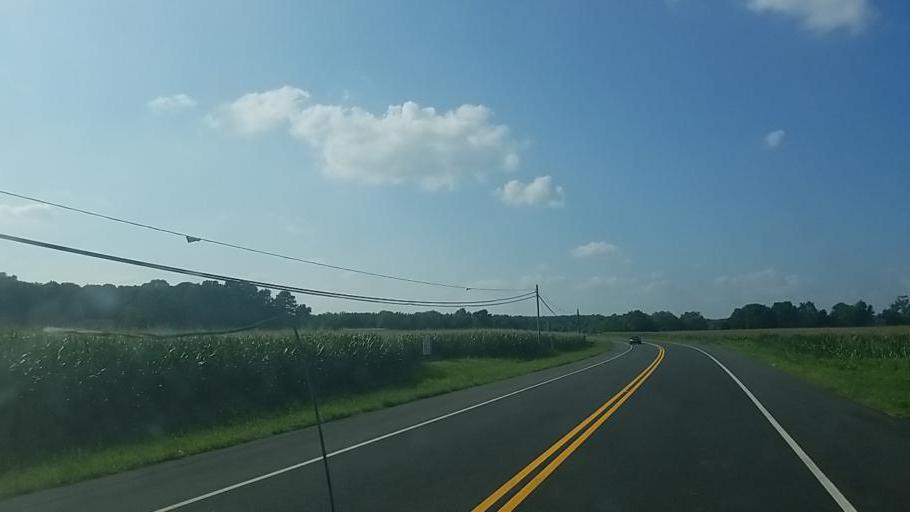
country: US
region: Maryland
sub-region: Worcester County
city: Ocean Pines
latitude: 38.3819
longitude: -75.2001
